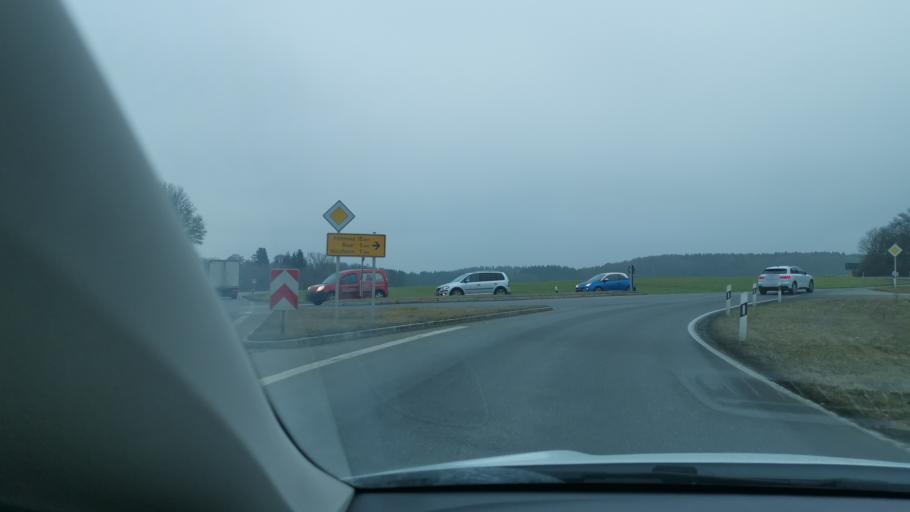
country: DE
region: Bavaria
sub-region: Swabia
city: Thierhaupten
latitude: 48.5759
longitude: 10.9076
